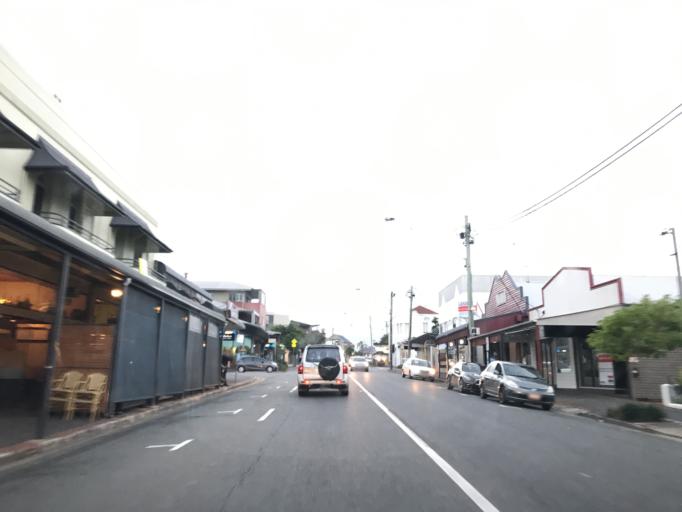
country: AU
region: Queensland
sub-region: Brisbane
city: Milton
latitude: -27.4616
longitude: 153.0055
